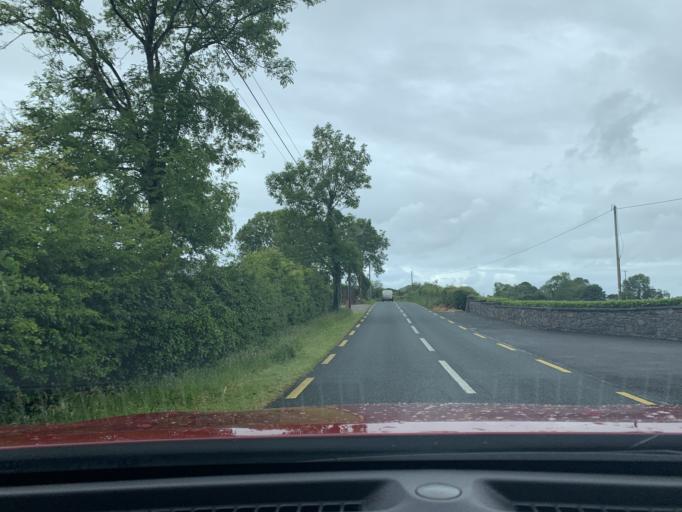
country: IE
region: Connaught
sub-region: Sligo
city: Sligo
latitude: 54.3123
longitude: -8.4590
